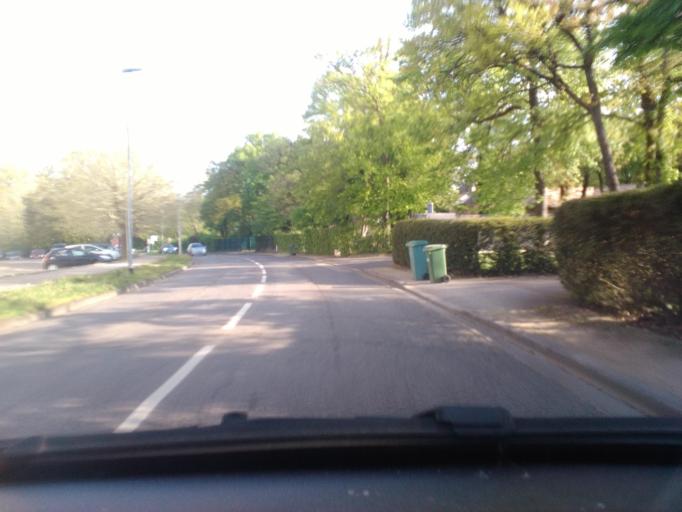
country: FR
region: Lorraine
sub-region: Departement de Meurthe-et-Moselle
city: Vandoeuvre-les-Nancy
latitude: 48.6493
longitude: 6.1600
